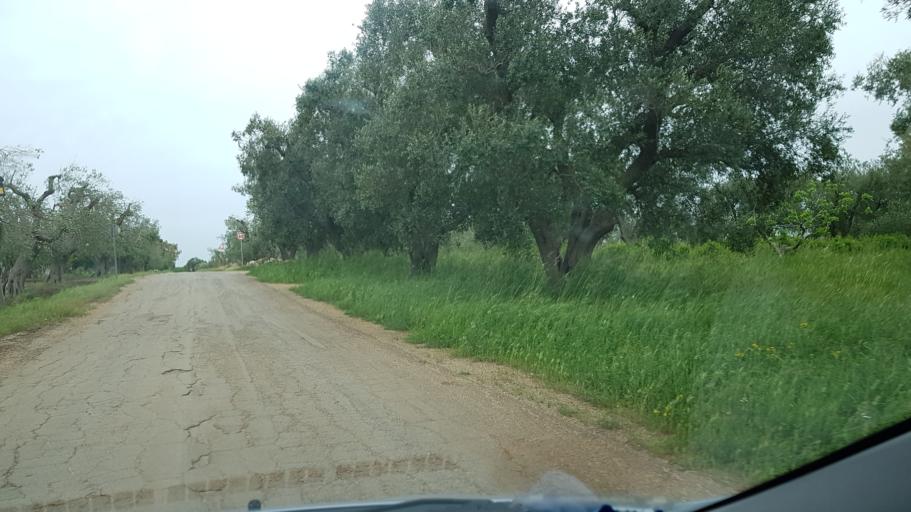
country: IT
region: Apulia
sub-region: Provincia di Brindisi
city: San Vito dei Normanni
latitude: 40.6209
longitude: 17.7689
